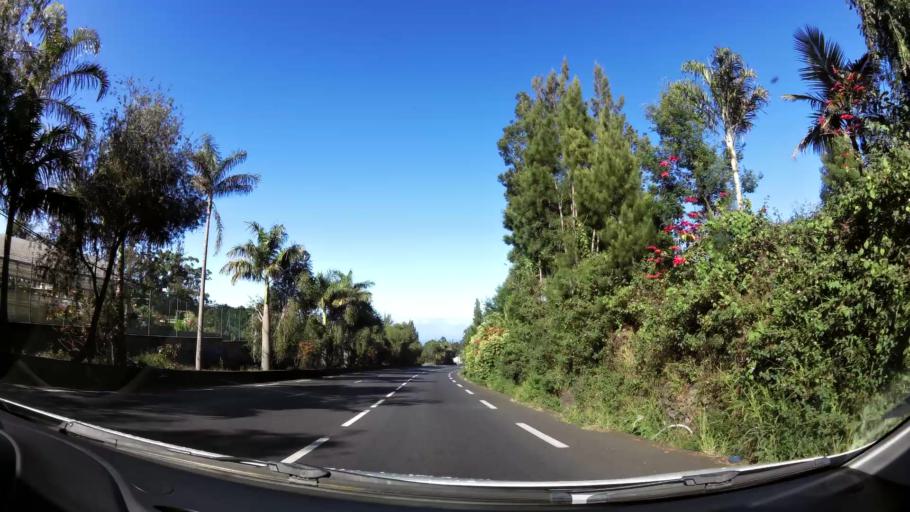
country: RE
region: Reunion
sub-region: Reunion
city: Le Tampon
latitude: -21.2384
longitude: 55.5300
